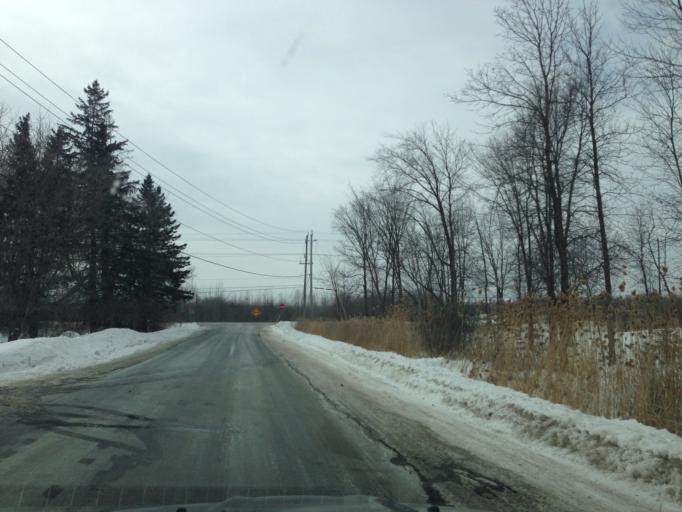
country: CA
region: Ontario
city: Ottawa
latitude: 45.3242
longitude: -75.5674
